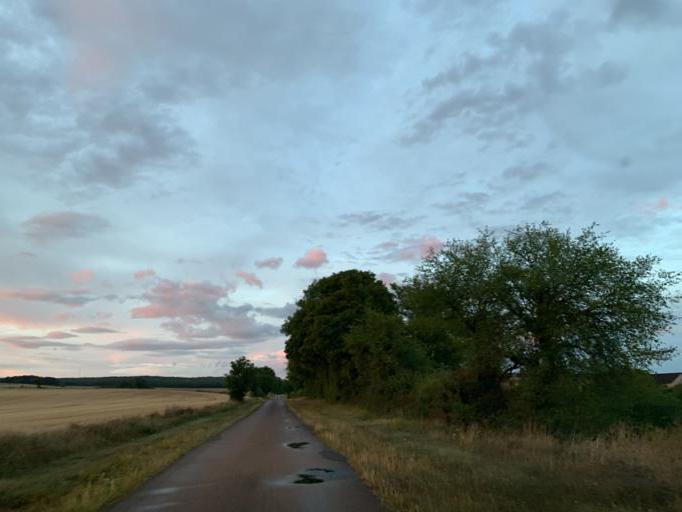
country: FR
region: Bourgogne
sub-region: Departement de l'Yonne
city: Fontenailles
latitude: 47.5523
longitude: 3.4270
